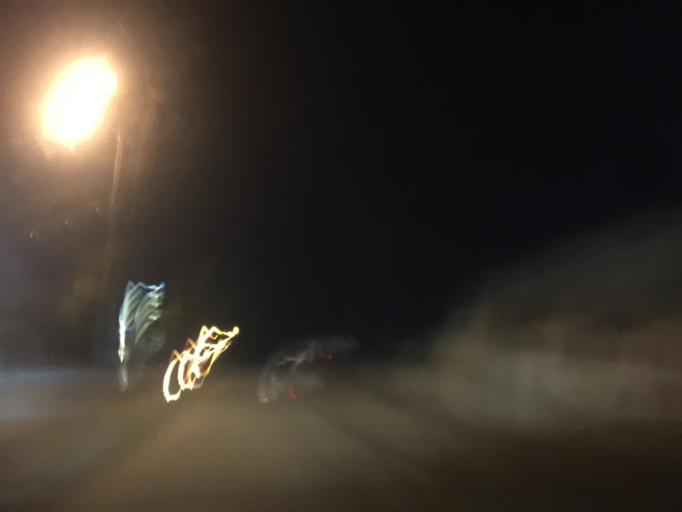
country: JO
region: Zarqa
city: Russeifa
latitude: 32.0326
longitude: 36.0461
